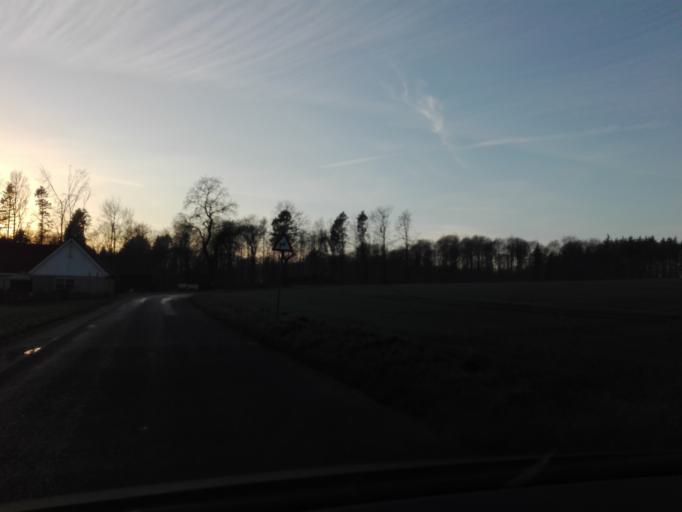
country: DK
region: Central Jutland
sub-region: Skanderborg Kommune
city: Galten
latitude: 56.1780
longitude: 9.9237
